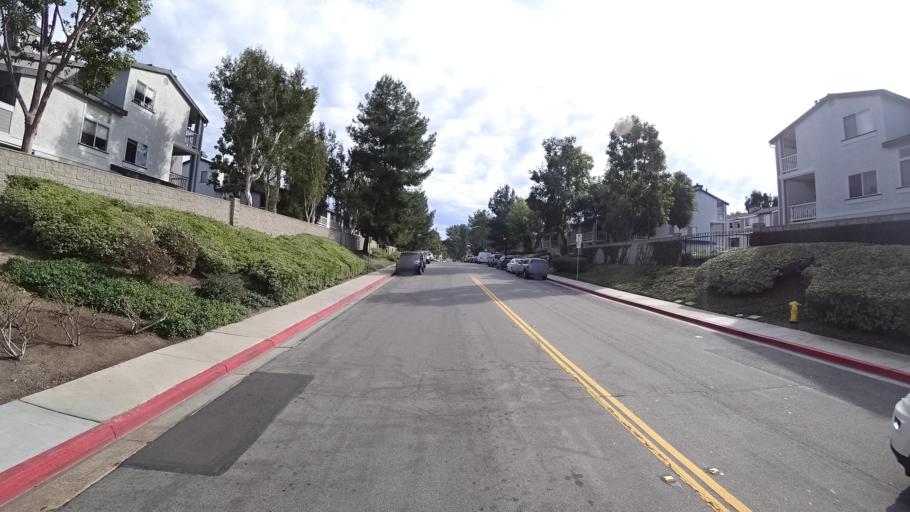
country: US
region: California
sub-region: Orange County
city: Aliso Viejo
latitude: 33.5773
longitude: -117.7104
